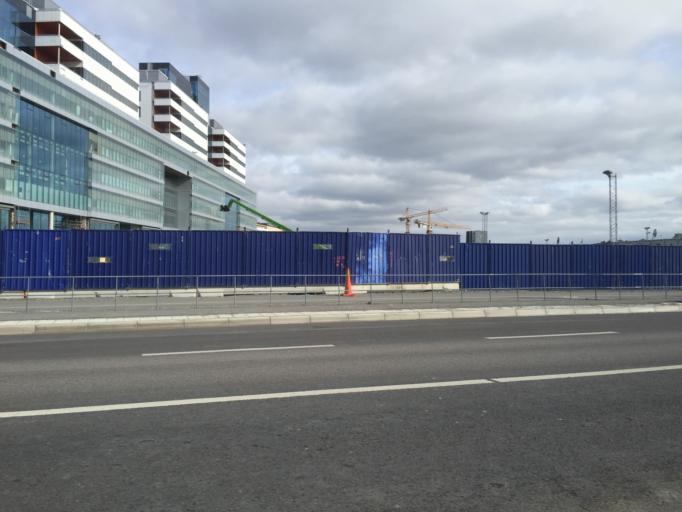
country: SE
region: Stockholm
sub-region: Solna Kommun
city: Solna
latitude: 59.3478
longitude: 18.0303
